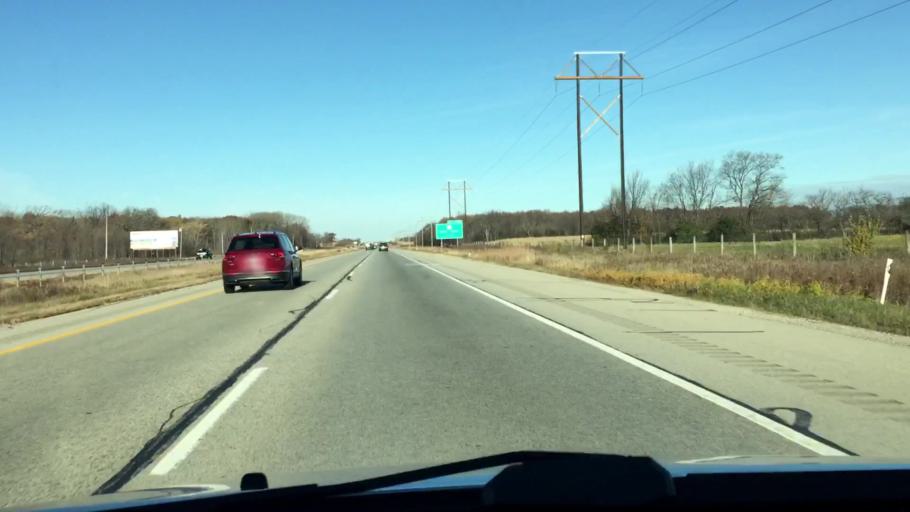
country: US
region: Wisconsin
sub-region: Fond du Lac County
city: North Fond du Lac
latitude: 43.8347
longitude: -88.5453
